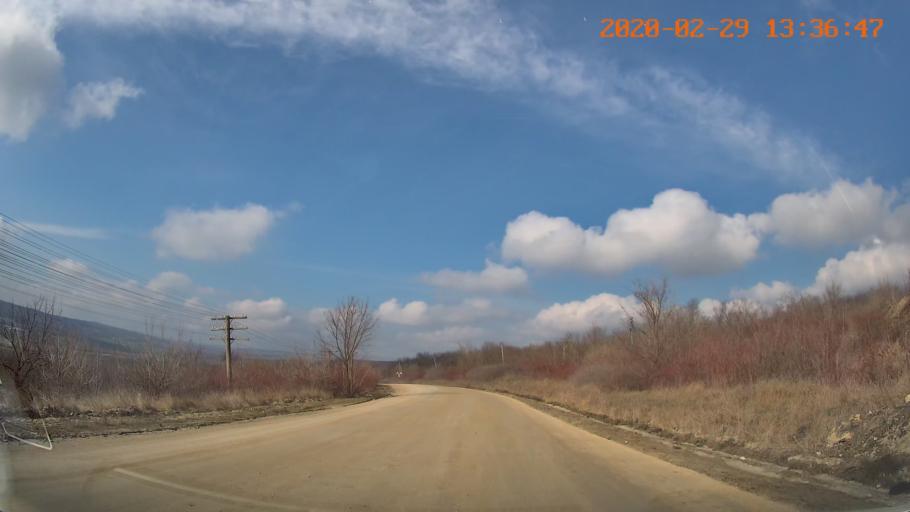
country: MD
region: Telenesti
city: Camenca
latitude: 47.8609
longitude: 28.6054
